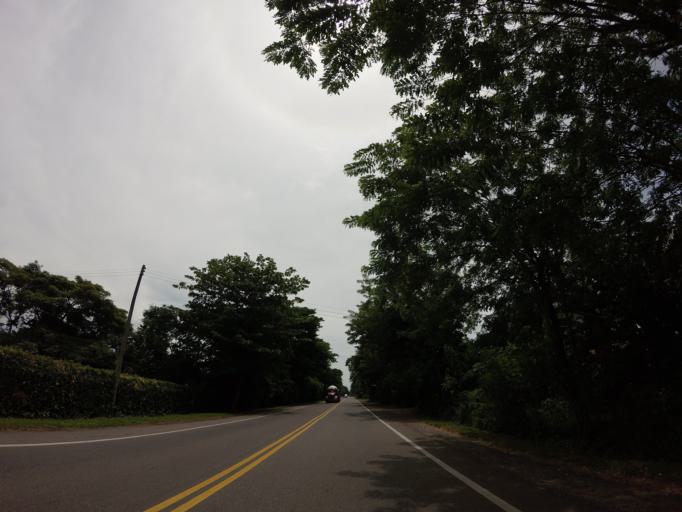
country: CO
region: Caldas
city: La Dorada
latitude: 5.4256
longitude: -74.6825
